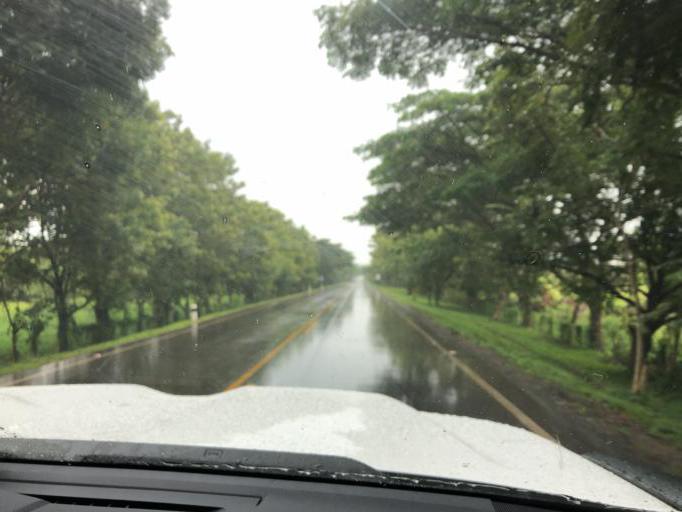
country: NI
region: Chontales
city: Villa Sandino
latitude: 12.0449
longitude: -84.9880
